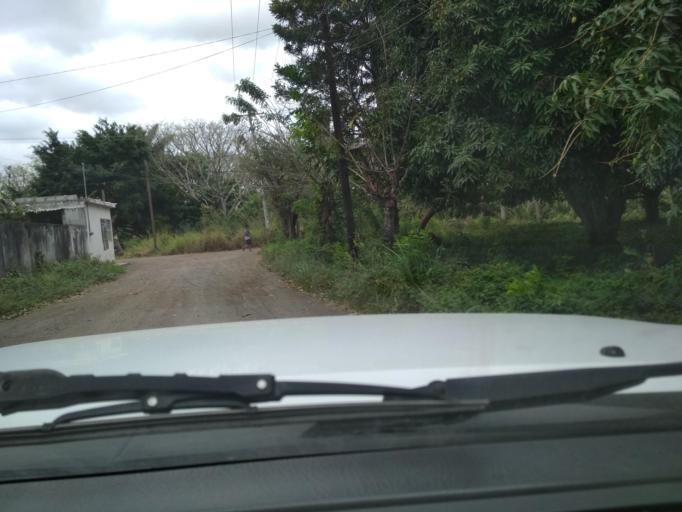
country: MX
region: Veracruz
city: Paso del Toro
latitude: 19.0522
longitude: -96.1343
